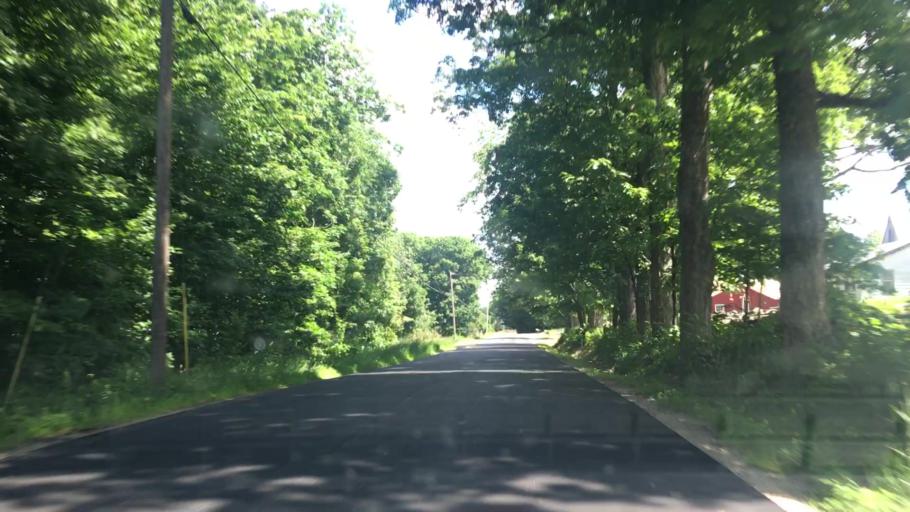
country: US
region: Maine
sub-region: Franklin County
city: Chesterville
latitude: 44.5687
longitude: -70.1475
